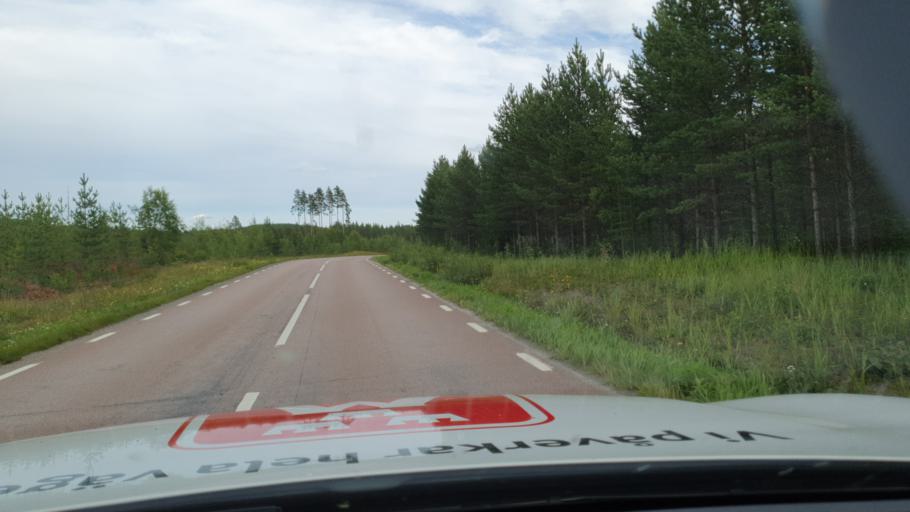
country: SE
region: Vaesternorrland
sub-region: Solleftea Kommun
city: As
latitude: 63.5669
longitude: 16.4363
